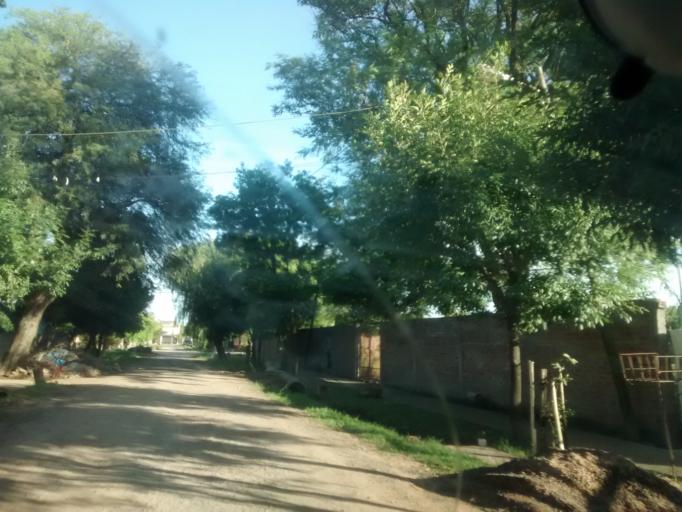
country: AR
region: Chaco
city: Resistencia
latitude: -27.4509
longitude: -59.0121
